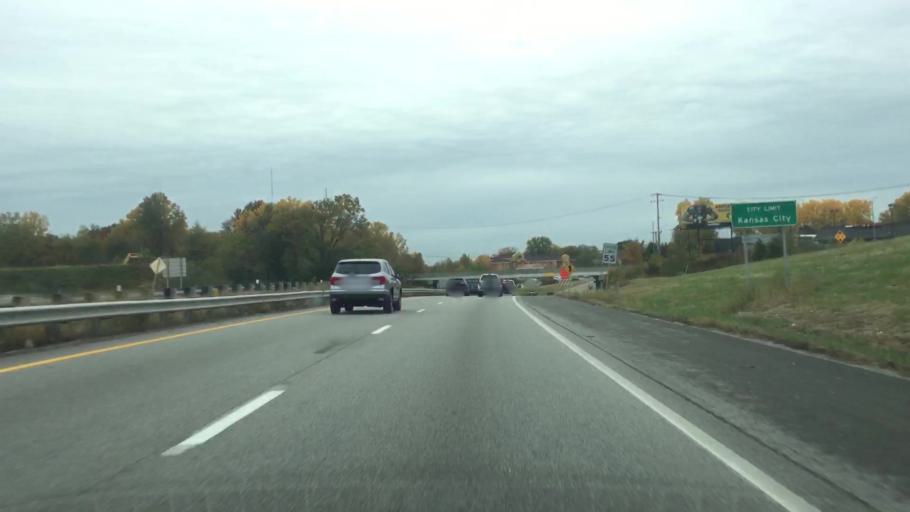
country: US
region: Missouri
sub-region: Jackson County
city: Raytown
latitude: 39.0011
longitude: -94.4828
